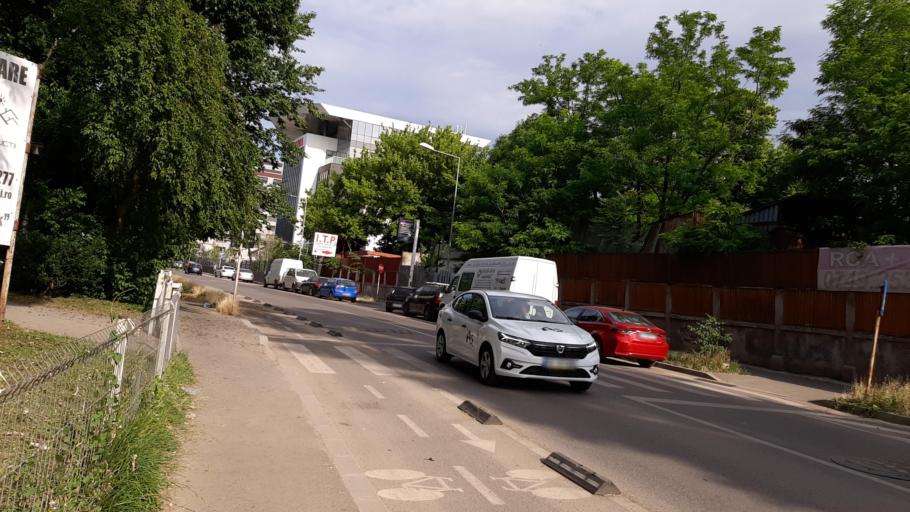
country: RO
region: Galati
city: Galati
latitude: 45.4394
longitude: 28.0323
